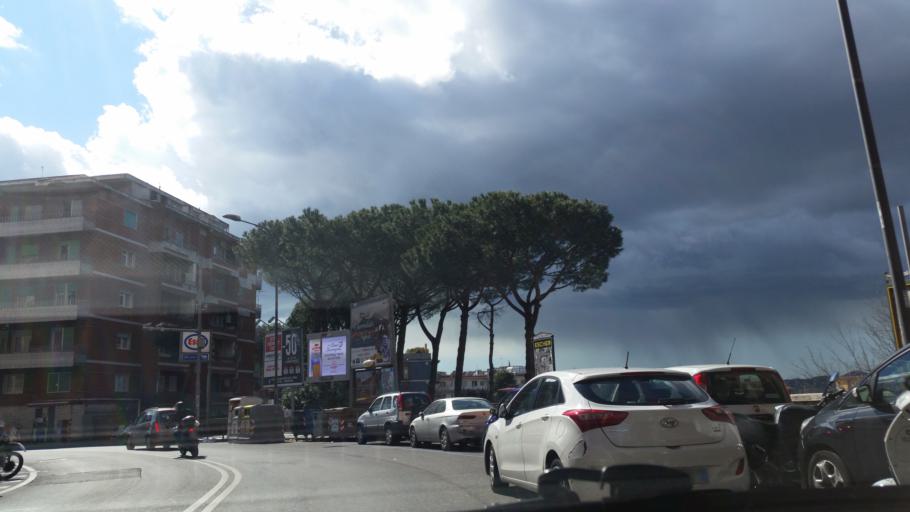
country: IT
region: Campania
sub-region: Provincia di Napoli
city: Napoli
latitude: 40.8414
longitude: 14.2177
